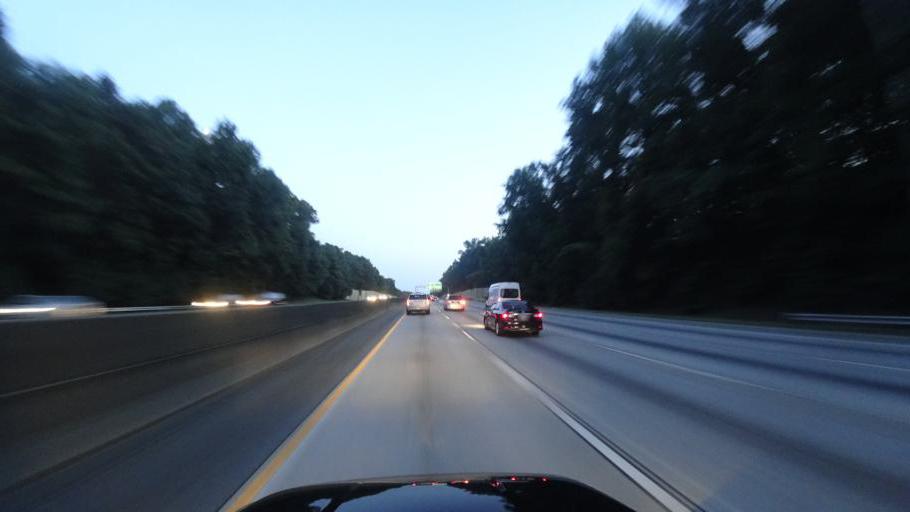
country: US
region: Georgia
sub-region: DeKalb County
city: Tucker
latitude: 33.8637
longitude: -84.2485
